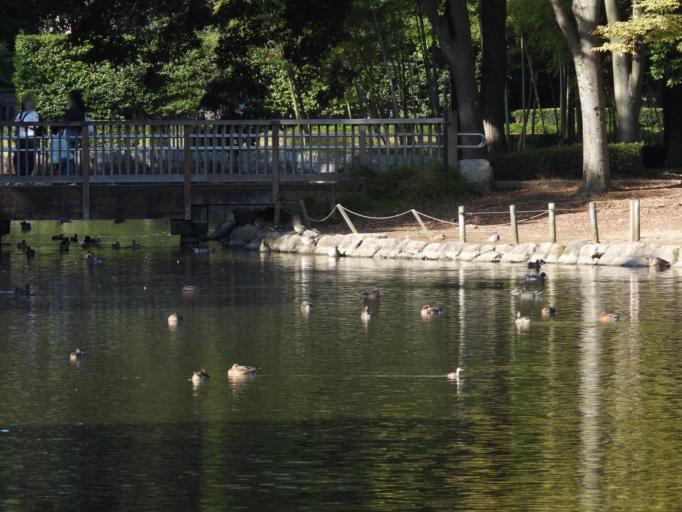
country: JP
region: Ibaraki
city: Naka
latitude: 36.0604
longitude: 140.1228
